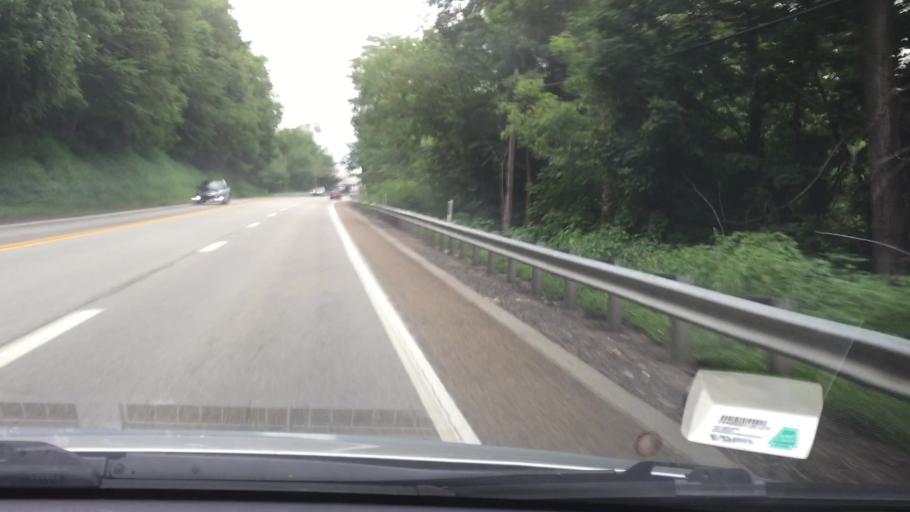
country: US
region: Pennsylvania
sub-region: Armstrong County
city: Freeport
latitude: 40.6836
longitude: -79.6962
